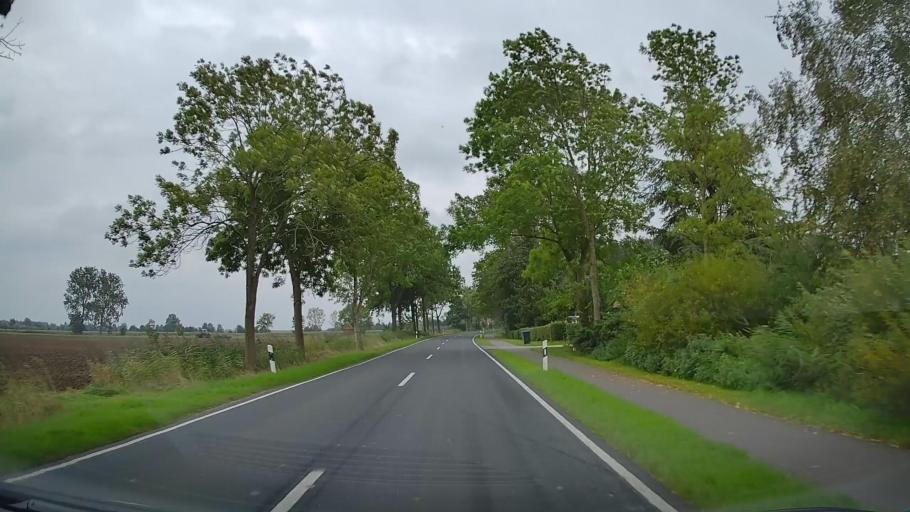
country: DE
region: Lower Saxony
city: Wischhafen
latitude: 53.8021
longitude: 9.3178
